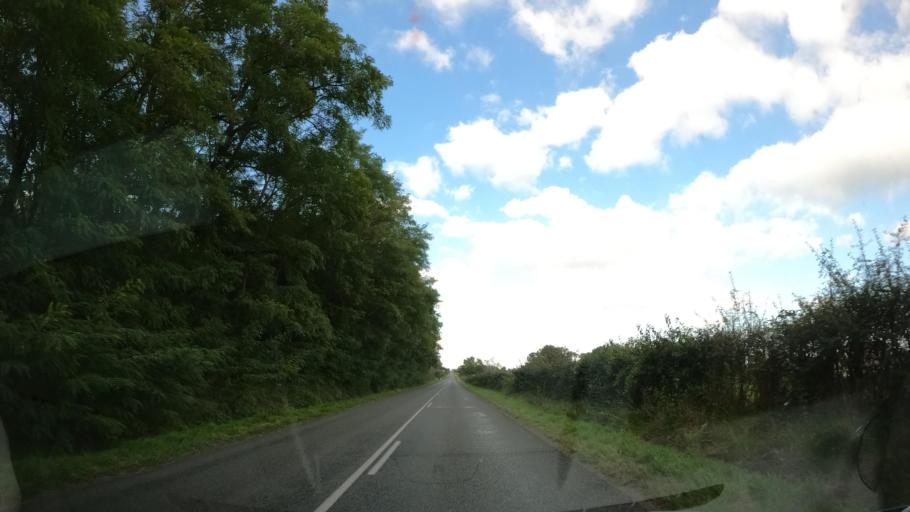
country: FR
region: Auvergne
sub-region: Departement de l'Allier
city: Dompierre-sur-Besbre
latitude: 46.5016
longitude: 3.6675
